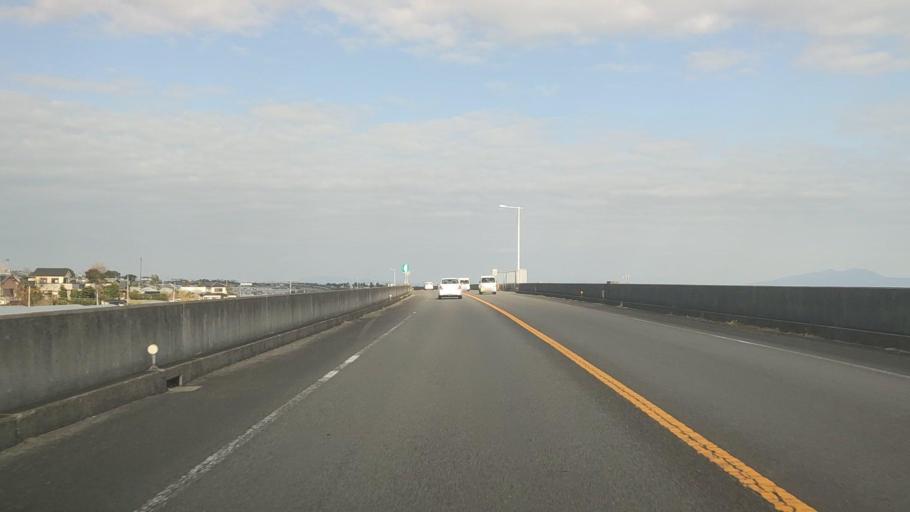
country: JP
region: Nagasaki
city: Shimabara
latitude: 32.7272
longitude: 130.3642
